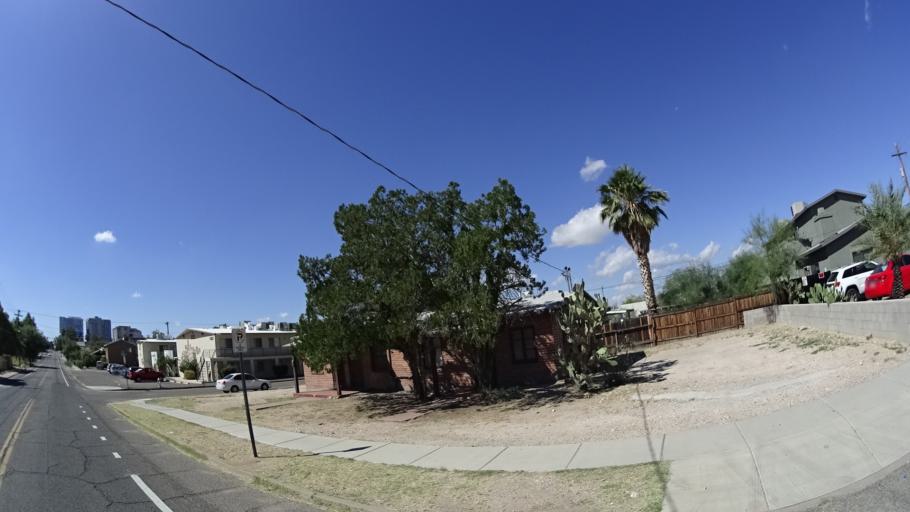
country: US
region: Arizona
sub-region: Pima County
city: Tucson
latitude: 32.2409
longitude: -110.9569
